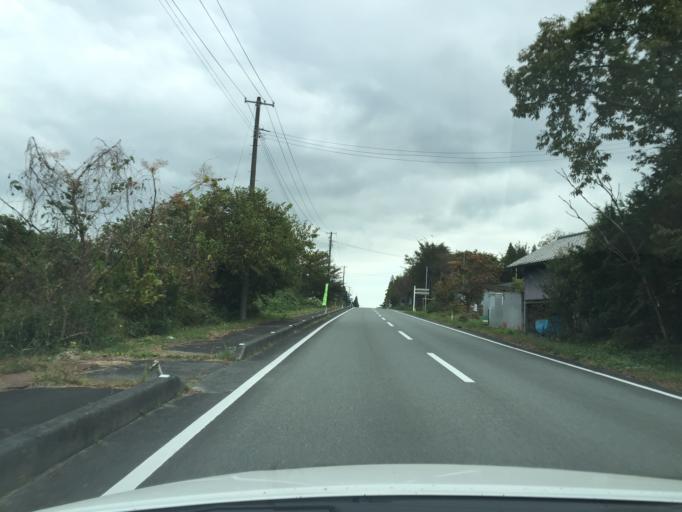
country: JP
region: Ibaraki
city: Kitaibaraki
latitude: 36.9309
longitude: 140.6905
